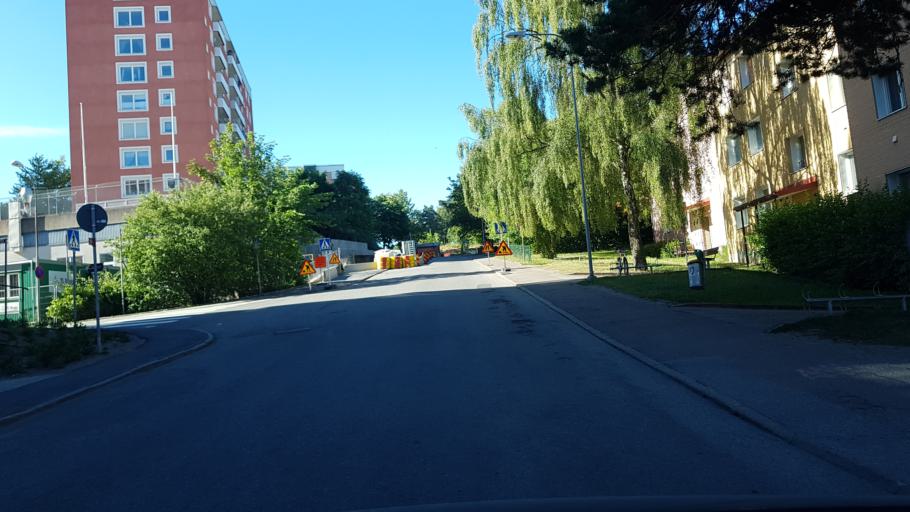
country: SE
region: Stockholm
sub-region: Jarfalla Kommun
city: Jakobsberg
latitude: 59.4183
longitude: 17.8392
